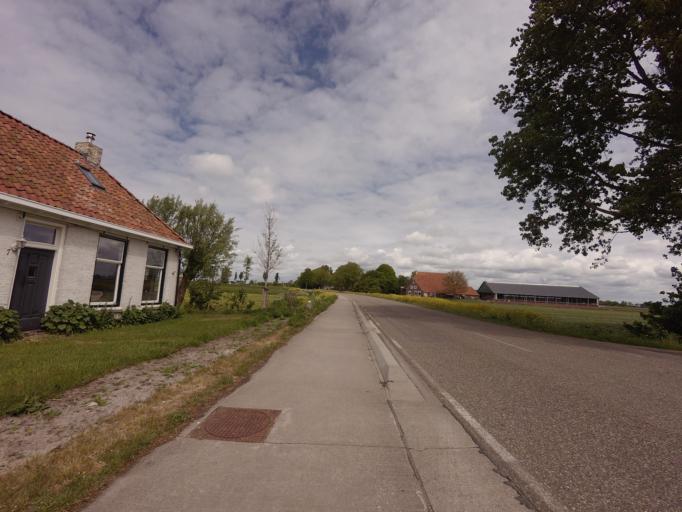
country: NL
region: Friesland
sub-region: Gemeente Gaasterlan-Sleat
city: Balk
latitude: 52.9157
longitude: 5.5409
